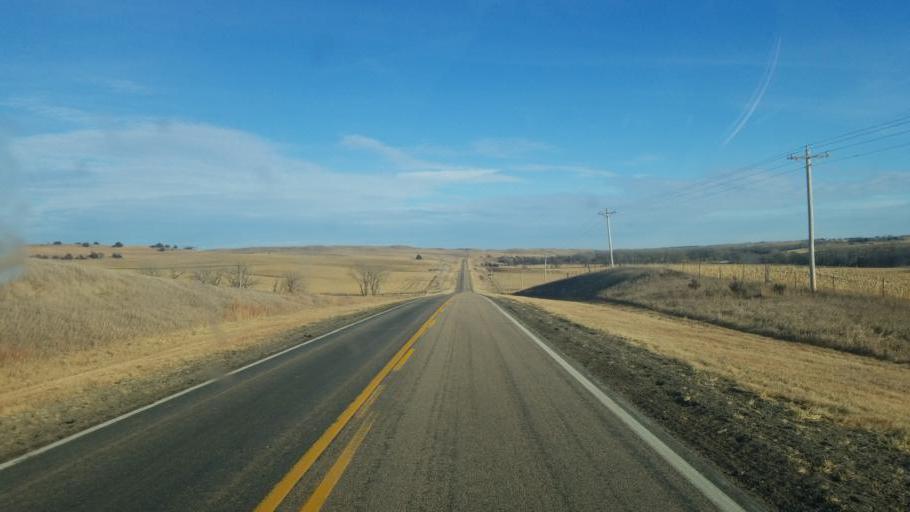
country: US
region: South Dakota
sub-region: Charles Mix County
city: Wagner
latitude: 42.8280
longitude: -98.3043
